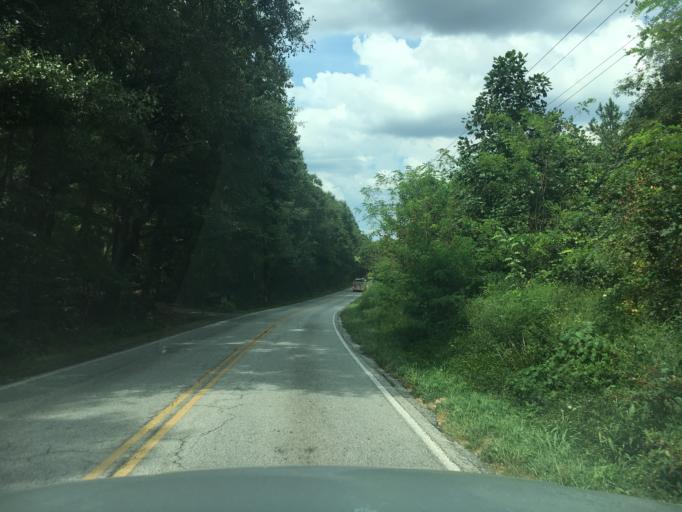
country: US
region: South Carolina
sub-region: Greenville County
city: Five Forks
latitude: 34.8372
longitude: -82.2278
